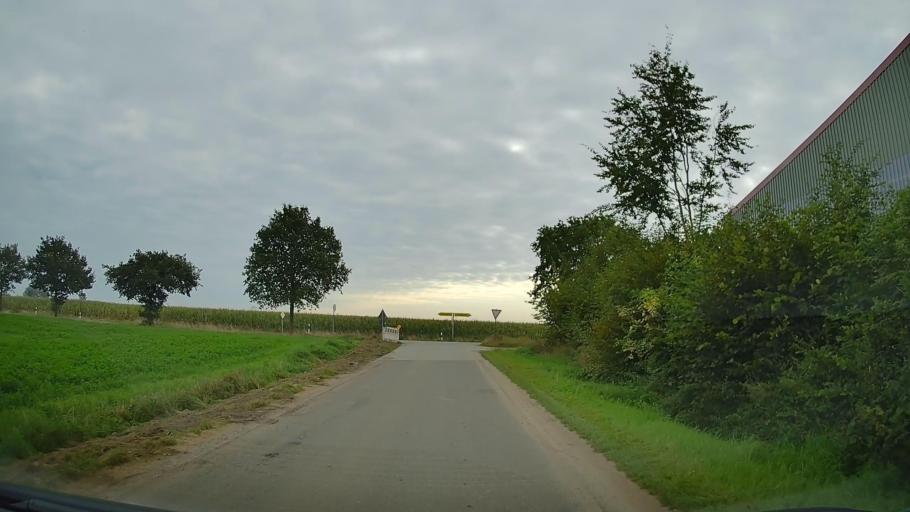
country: DE
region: Schleswig-Holstein
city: Hohenfelde
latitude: 54.3671
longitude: 10.5419
